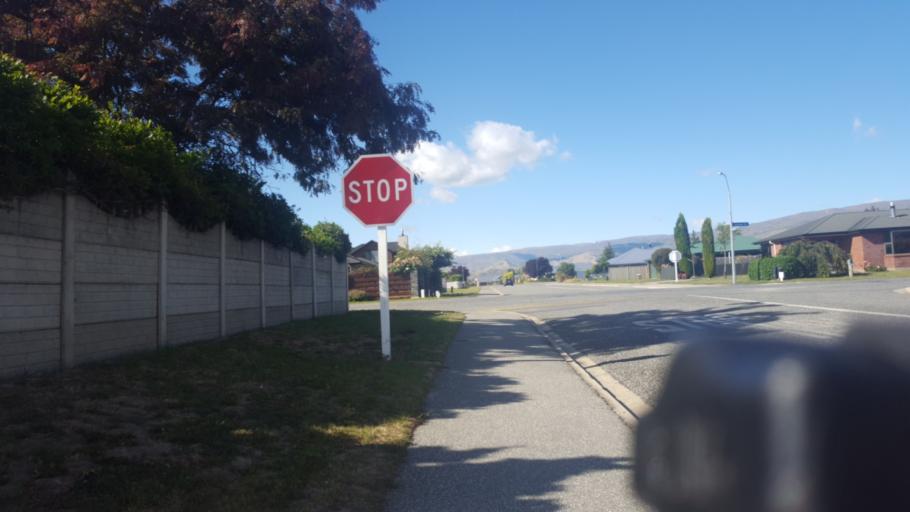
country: NZ
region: Otago
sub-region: Queenstown-Lakes District
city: Wanaka
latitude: -45.0466
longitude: 169.1998
